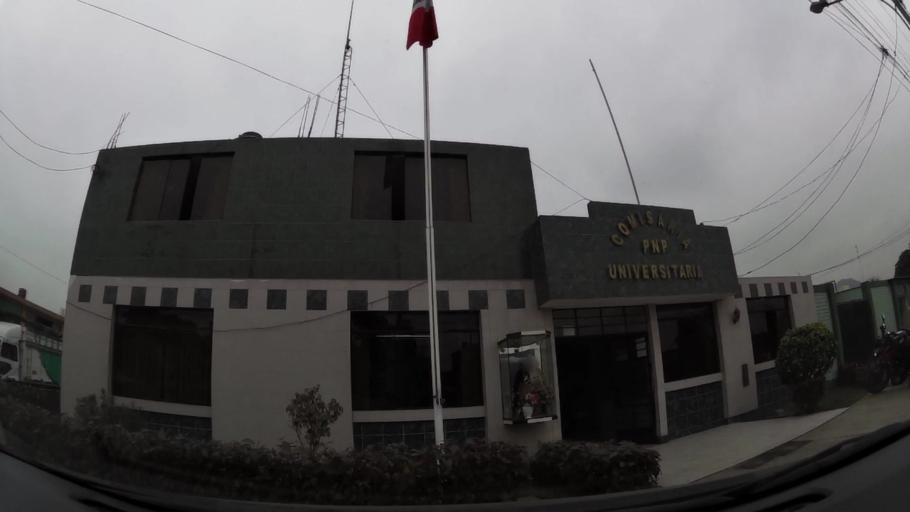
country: PE
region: Lima
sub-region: Lima
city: Independencia
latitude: -11.9473
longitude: -77.0601
